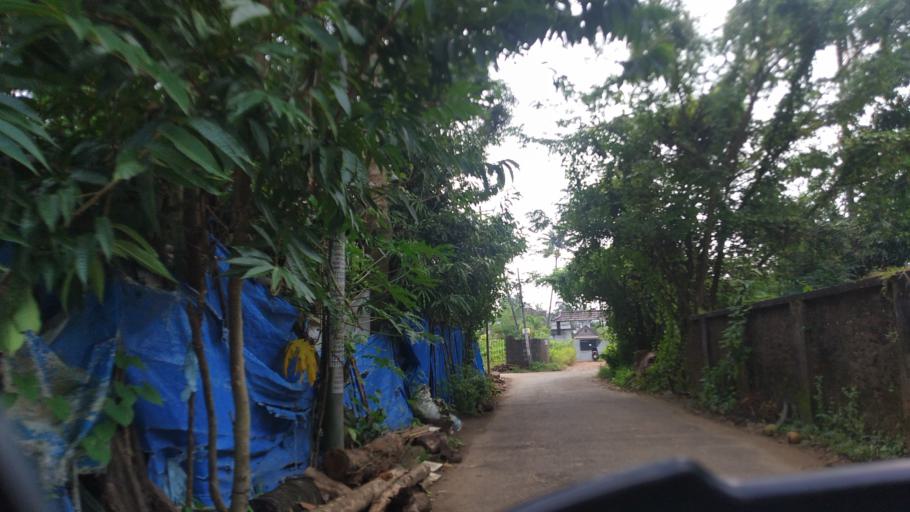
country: IN
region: Kerala
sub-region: Ernakulam
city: Elur
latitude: 10.0533
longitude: 76.2190
